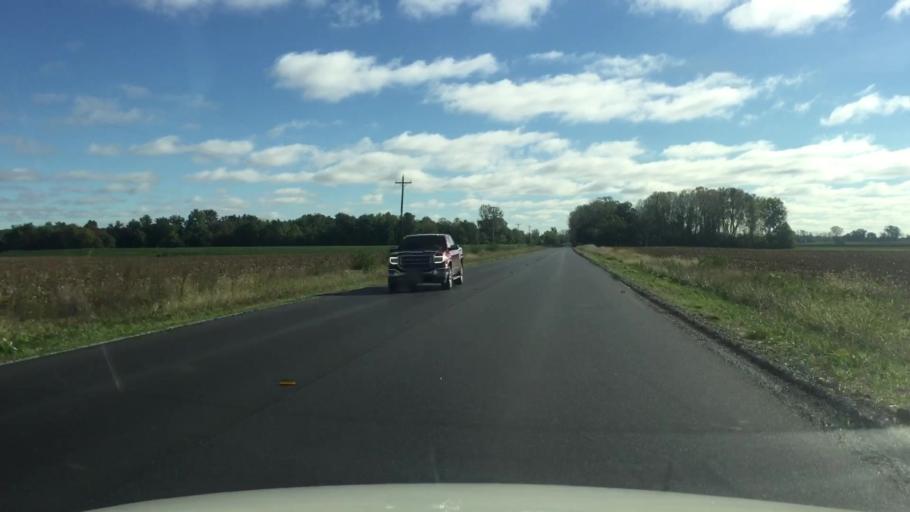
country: US
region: Missouri
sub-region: Howard County
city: New Franklin
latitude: 39.0030
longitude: -92.7222
